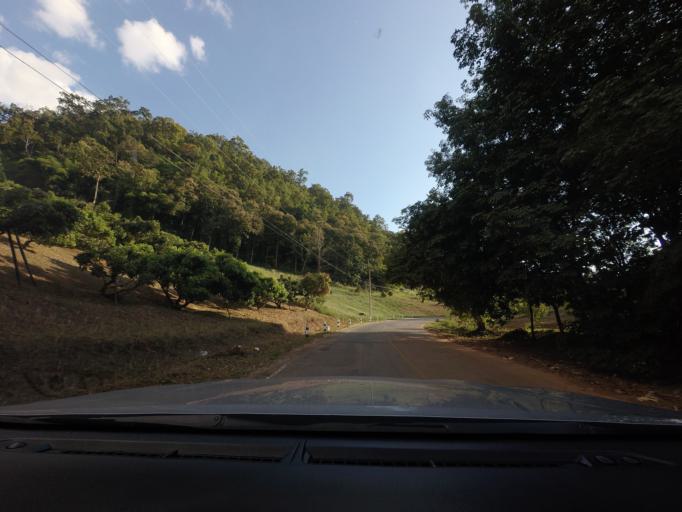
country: TH
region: Chiang Mai
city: Chai Prakan
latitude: 19.6213
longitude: 99.1661
